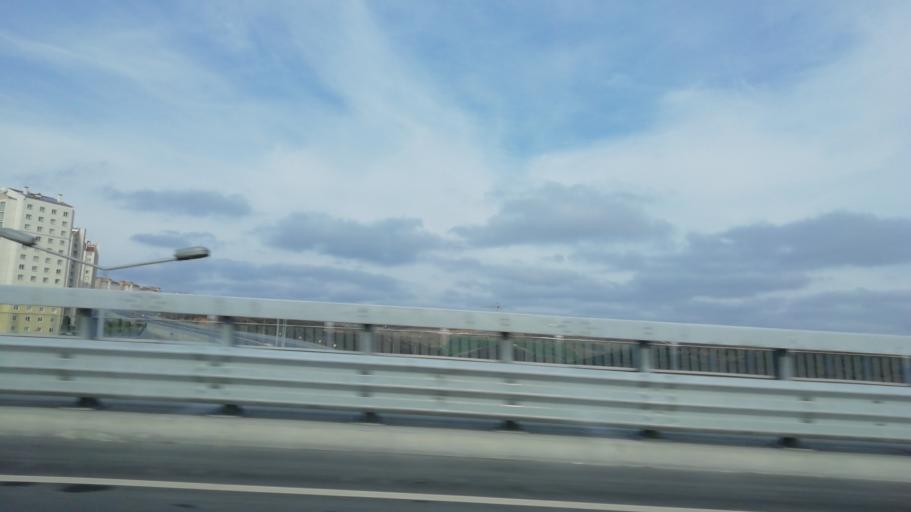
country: TR
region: Istanbul
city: Basaksehir
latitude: 41.1292
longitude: 28.7905
